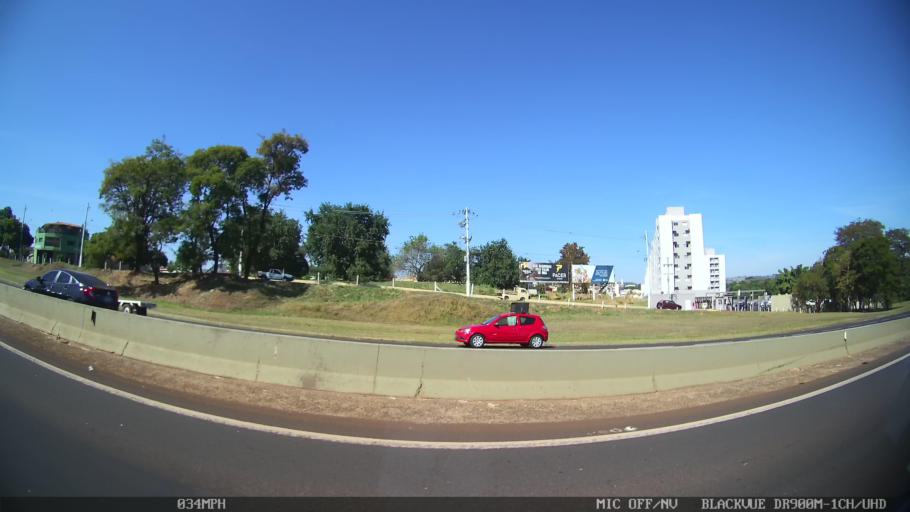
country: BR
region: Sao Paulo
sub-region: Ribeirao Preto
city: Ribeirao Preto
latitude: -21.2133
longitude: -47.7722
